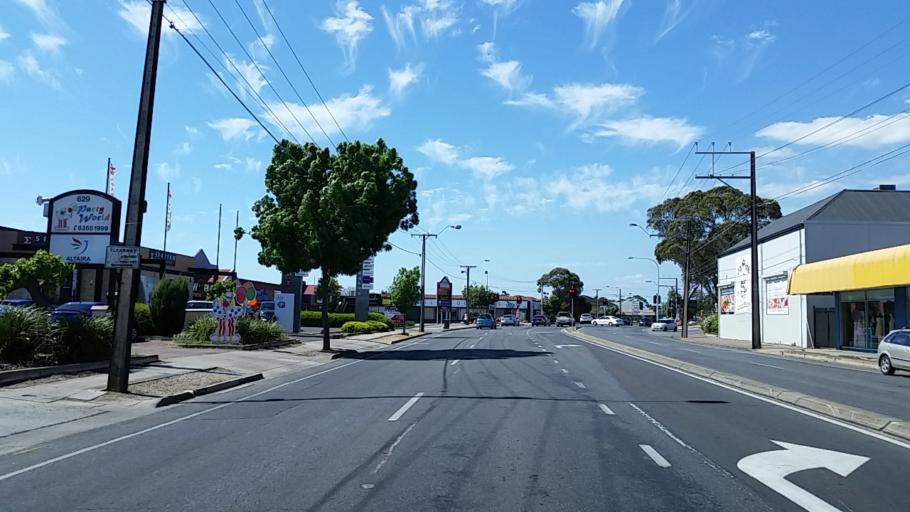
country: AU
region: South Australia
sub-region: Campbelltown
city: Paradise
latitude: -34.8775
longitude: 138.6640
